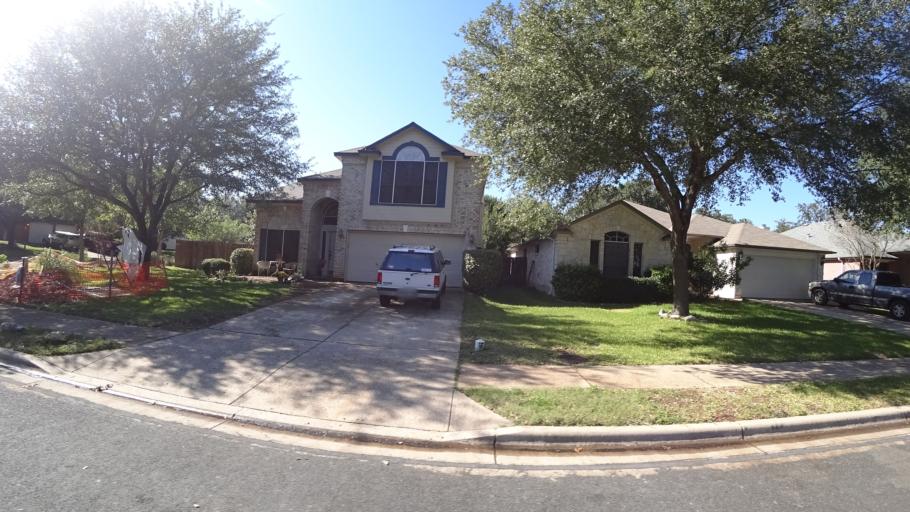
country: US
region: Texas
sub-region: Travis County
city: Shady Hollow
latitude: 30.1999
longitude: -97.8581
